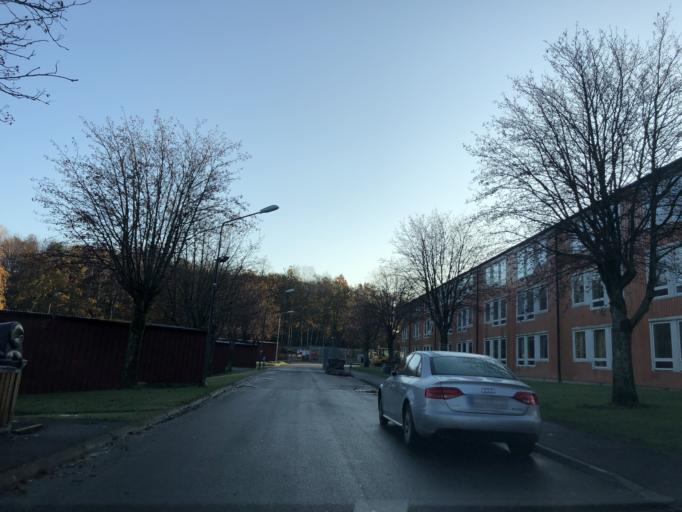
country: SE
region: Vaestra Goetaland
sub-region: Goteborg
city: Hammarkullen
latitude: 57.7831
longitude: 12.0369
